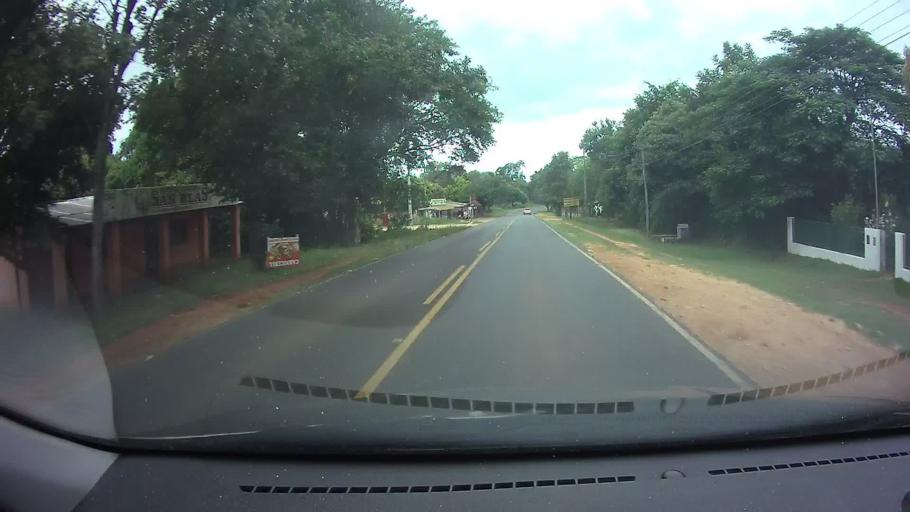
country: PY
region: Central
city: Guarambare
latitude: -25.5446
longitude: -57.4994
